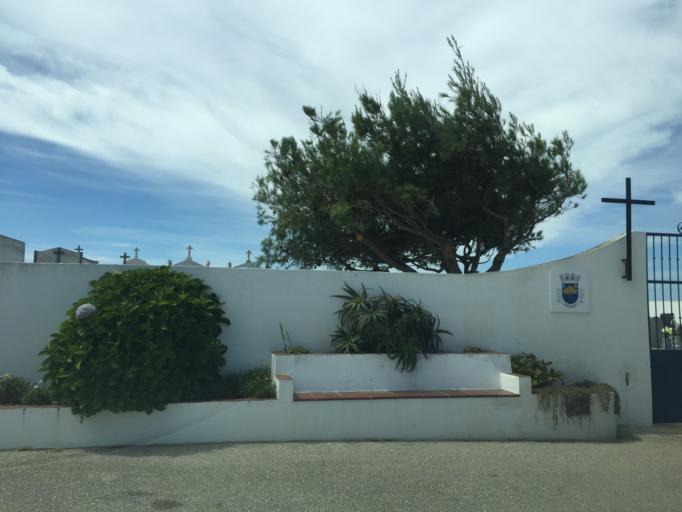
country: PT
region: Lisbon
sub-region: Lourinha
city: Lourinha
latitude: 39.2066
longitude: -9.3409
